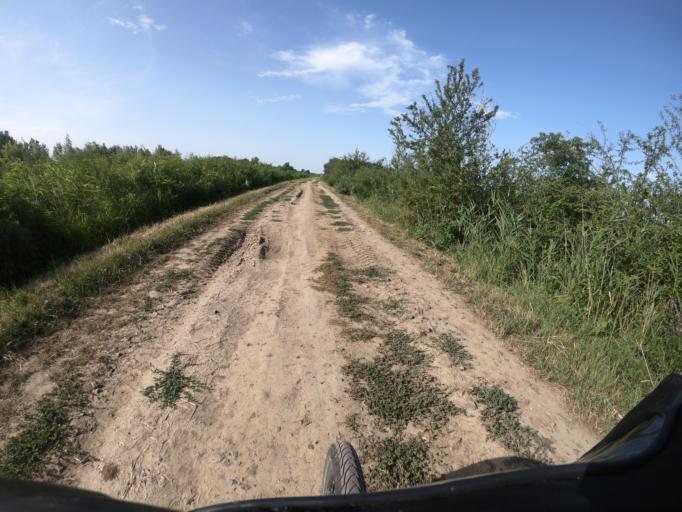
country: HU
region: Hajdu-Bihar
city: Tiszacsege
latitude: 47.6076
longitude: 20.9981
